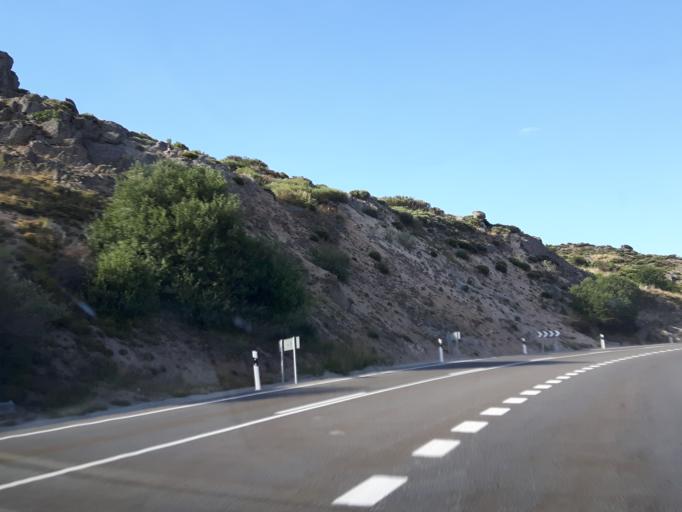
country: ES
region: Castille and Leon
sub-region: Provincia de Avila
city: Mengamunoz
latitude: 40.4803
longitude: -5.0082
